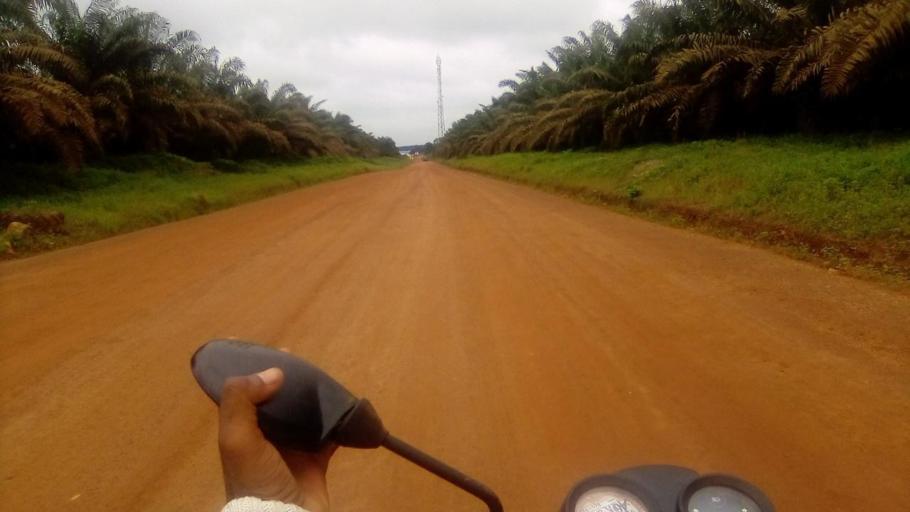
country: SL
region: Southern Province
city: Tongole
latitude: 7.4314
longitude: -11.8488
